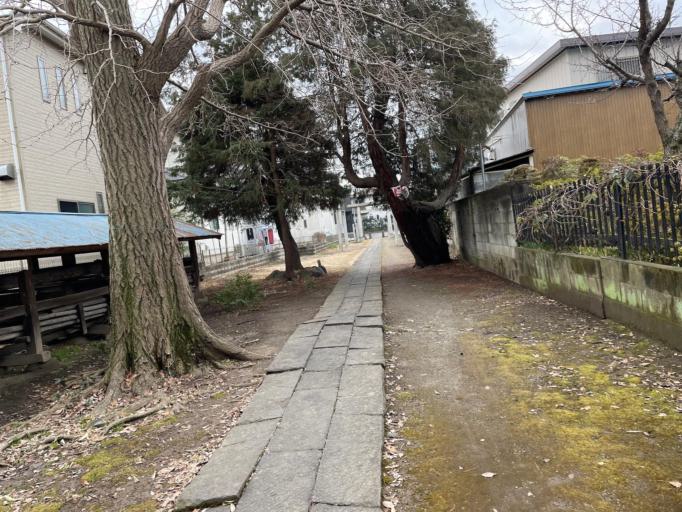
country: JP
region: Saitama
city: Yoshikawa
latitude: 35.8542
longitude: 139.8448
